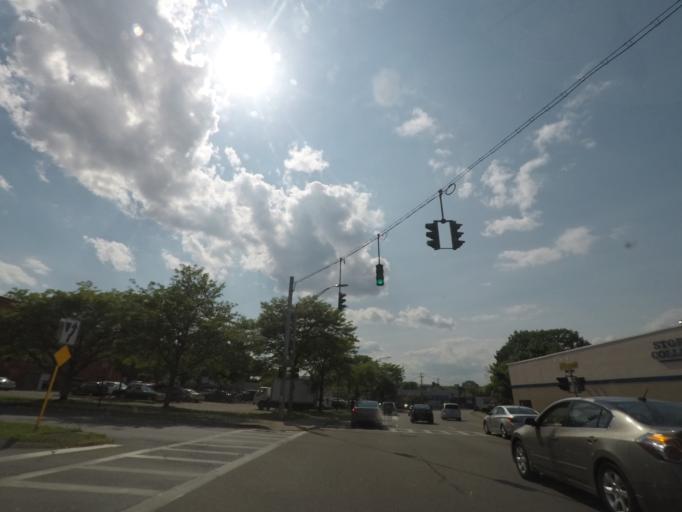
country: US
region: New York
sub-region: Dutchess County
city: Poughkeepsie
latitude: 41.7025
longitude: -73.9205
